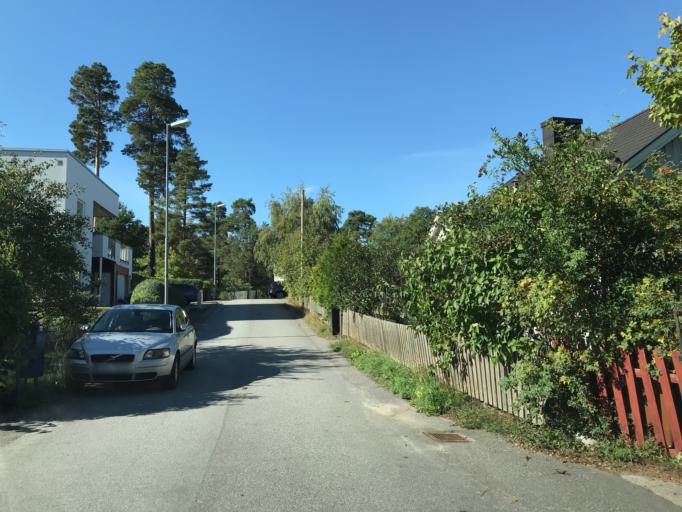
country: SE
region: Stockholm
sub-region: Sollentuna Kommun
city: Sollentuna
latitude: 59.4271
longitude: 17.9622
